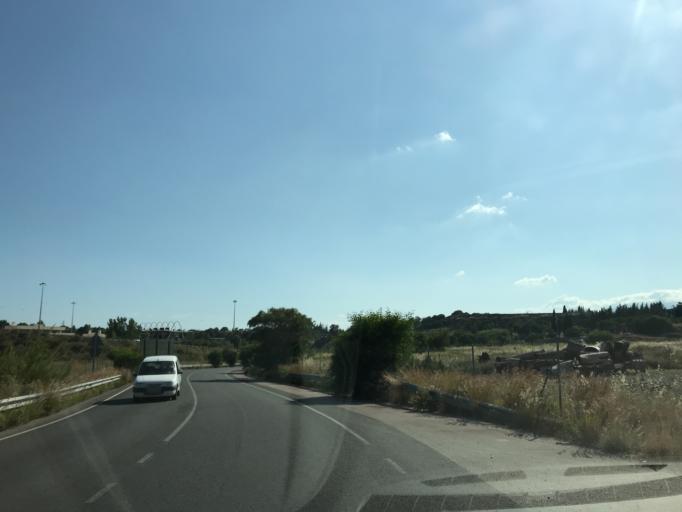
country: ES
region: Andalusia
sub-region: Provincia de Malaga
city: Benahavis
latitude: 36.5020
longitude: -5.0062
